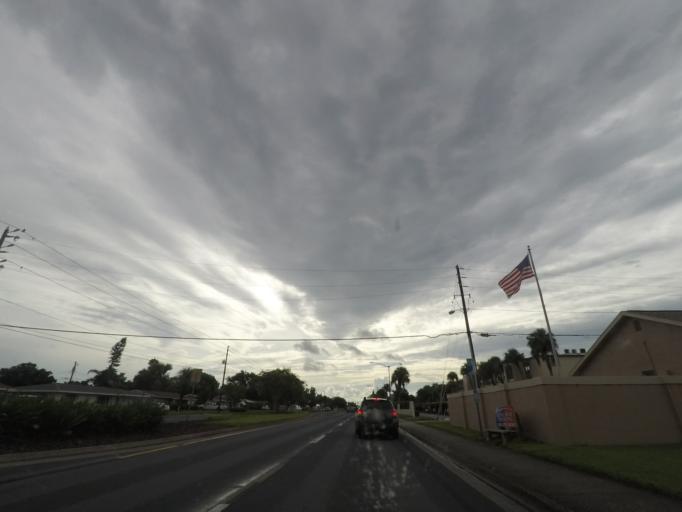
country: US
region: Florida
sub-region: Pinellas County
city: Seminole
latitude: 27.8434
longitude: -82.8020
